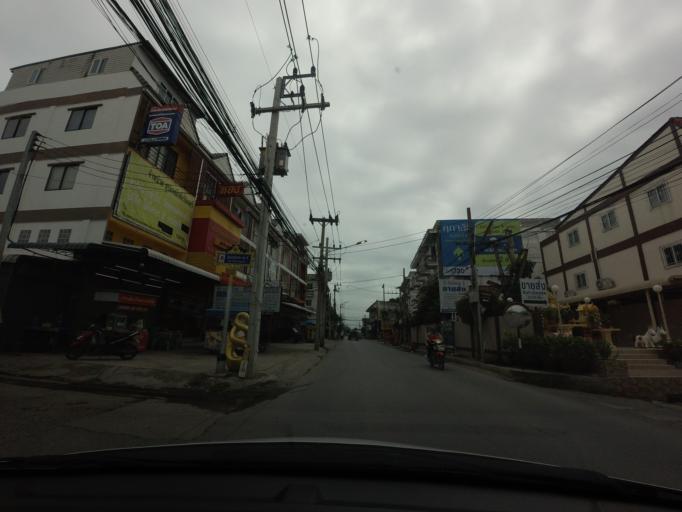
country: TH
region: Pathum Thani
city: Lam Luk Ka
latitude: 13.9313
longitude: 100.7502
